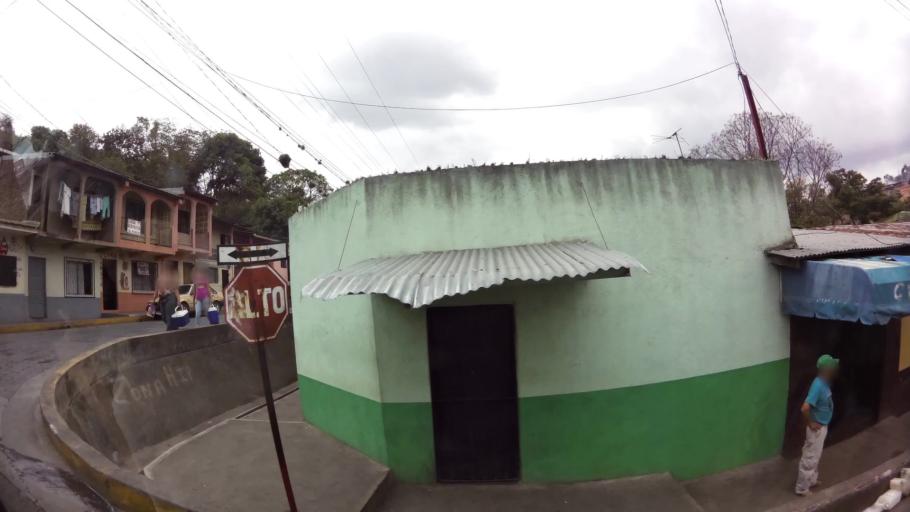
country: NI
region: Matagalpa
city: Matagalpa
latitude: 12.9330
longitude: -85.9116
